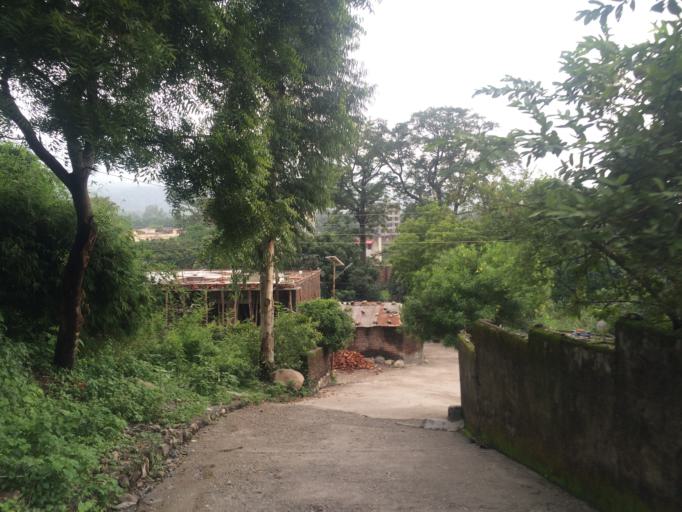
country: IN
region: Uttarakhand
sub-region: Dehradun
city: Birbhaddar
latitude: 30.0743
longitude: 78.2782
